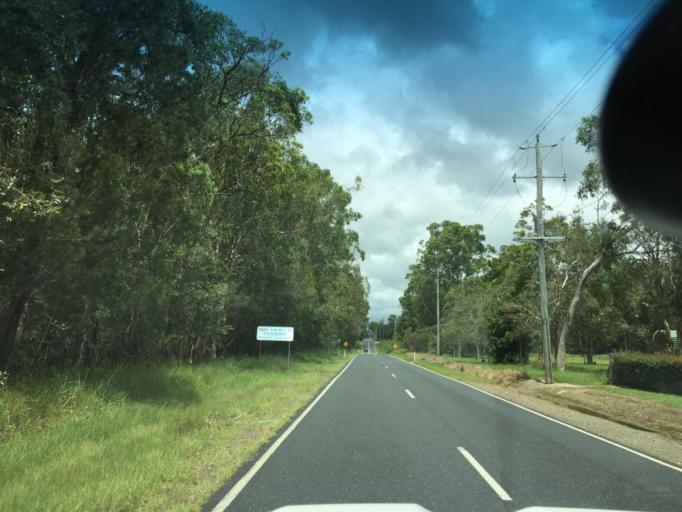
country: AU
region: Queensland
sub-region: Moreton Bay
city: Caboolture
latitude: -27.0486
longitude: 152.9121
